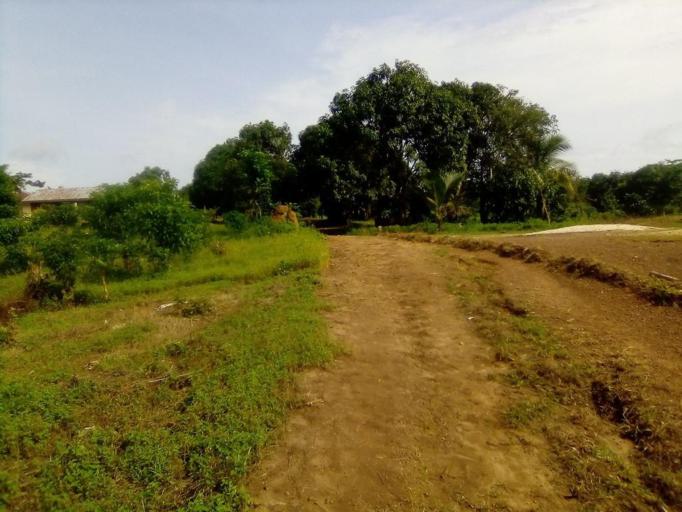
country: SL
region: Southern Province
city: Pujehun
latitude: 7.3632
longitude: -11.7260
